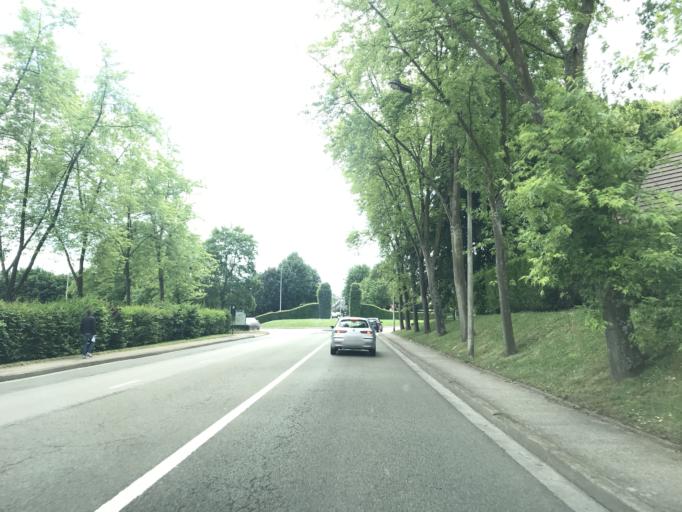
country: FR
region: Haute-Normandie
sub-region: Departement de la Seine-Maritime
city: Mont-Saint-Aignan
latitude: 49.4698
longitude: 1.0909
